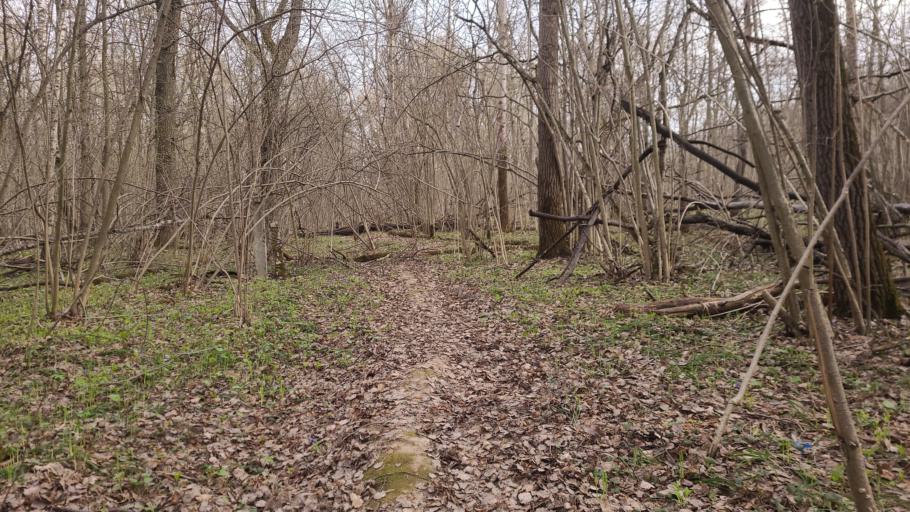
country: RU
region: Moskovskaya
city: Belyye Stolby
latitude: 55.3142
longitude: 37.8720
